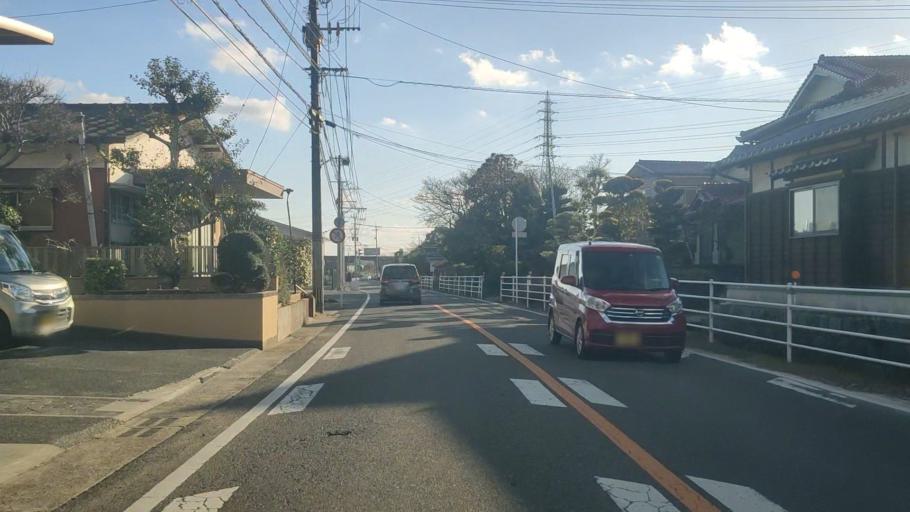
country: JP
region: Saga Prefecture
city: Saga-shi
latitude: 33.3219
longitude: 130.2676
